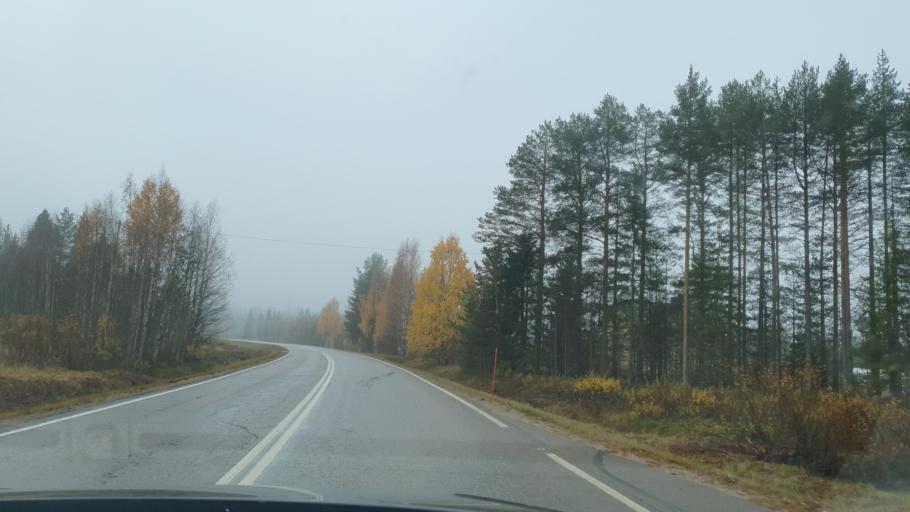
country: FI
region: Lapland
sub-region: Rovaniemi
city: Rovaniemi
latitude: 66.8187
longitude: 25.3950
